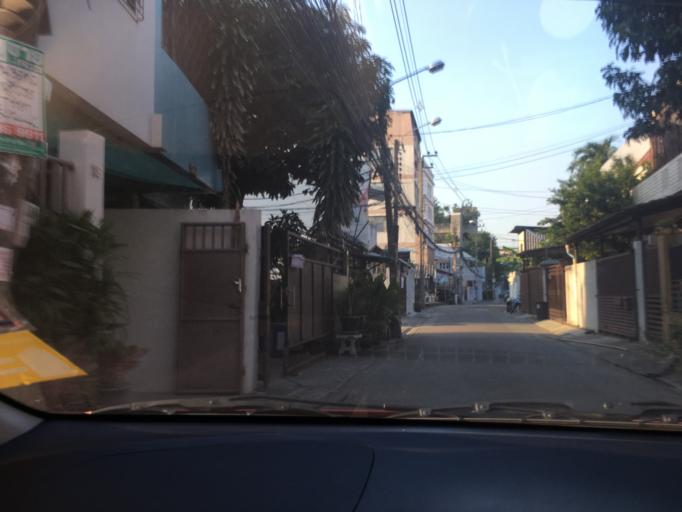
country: TH
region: Bangkok
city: Huai Khwang
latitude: 13.8011
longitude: 100.5784
